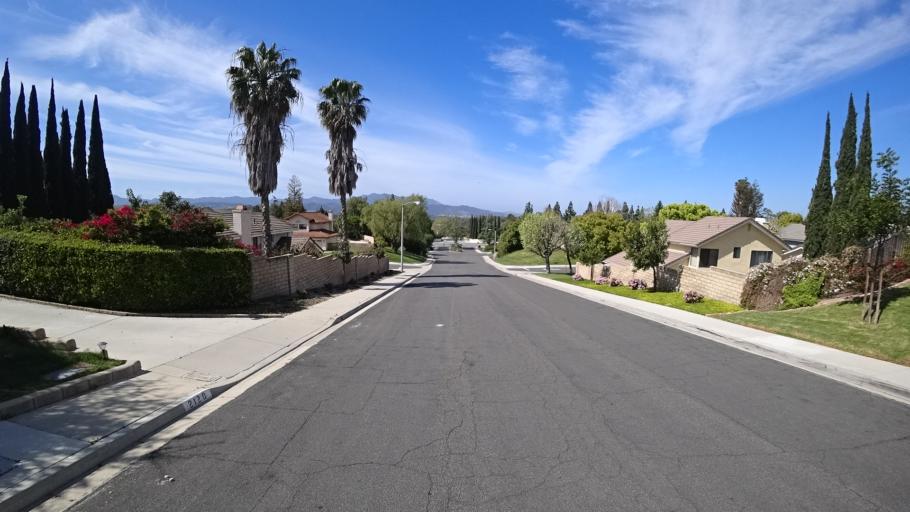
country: US
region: California
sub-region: Ventura County
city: Thousand Oaks
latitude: 34.2148
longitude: -118.8395
